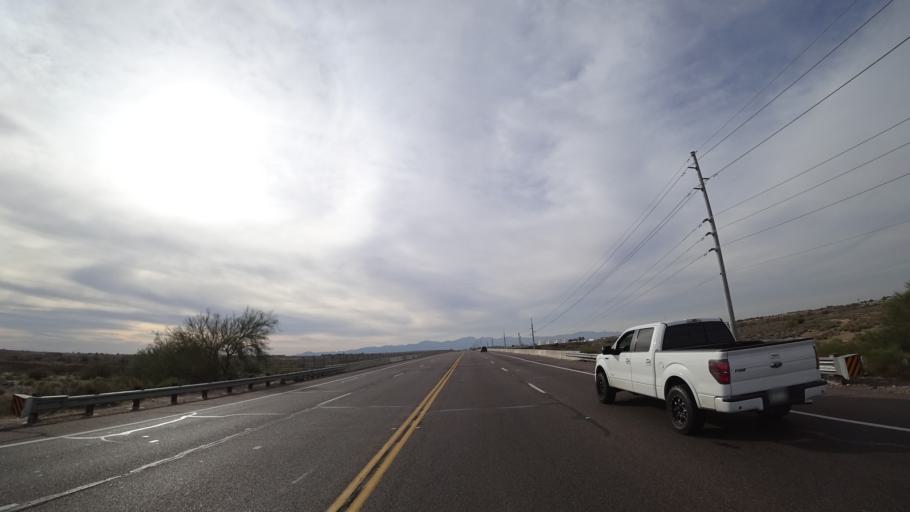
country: US
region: Arizona
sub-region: Maricopa County
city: Youngtown
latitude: 33.5654
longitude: -112.3128
